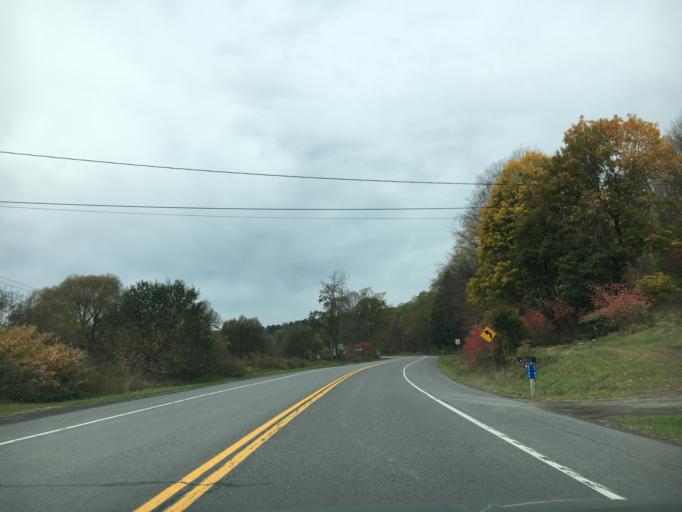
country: US
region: New York
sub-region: Otsego County
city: Oneonta
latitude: 42.5289
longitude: -74.9726
